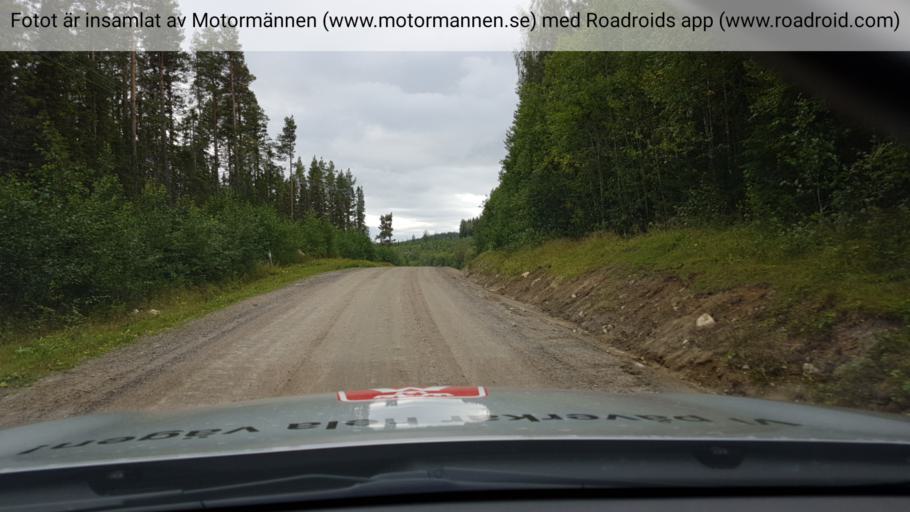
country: SE
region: Jaemtland
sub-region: Ragunda Kommun
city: Hammarstrand
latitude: 62.9106
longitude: 16.0955
